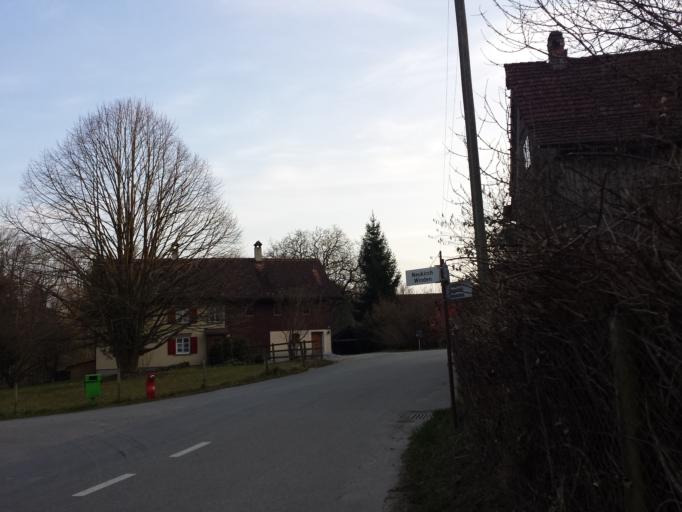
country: CH
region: Thurgau
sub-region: Arbon District
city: Egnach
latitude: 47.5345
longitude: 9.3625
